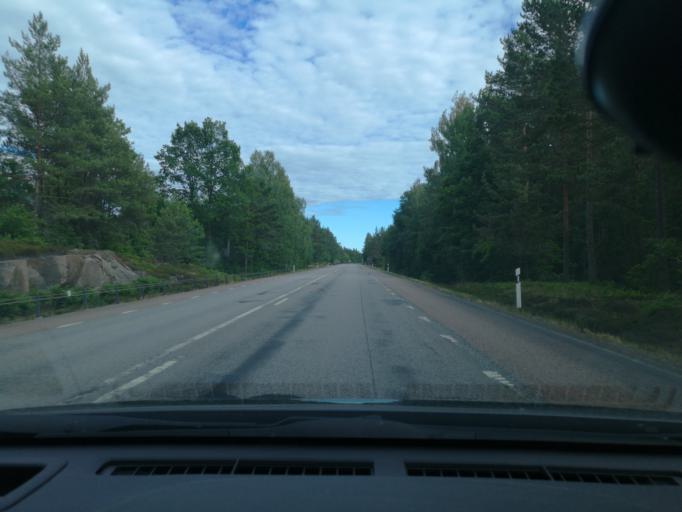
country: SE
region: Kalmar
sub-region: Vasterviks Kommun
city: Ankarsrum
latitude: 57.6387
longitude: 16.4481
